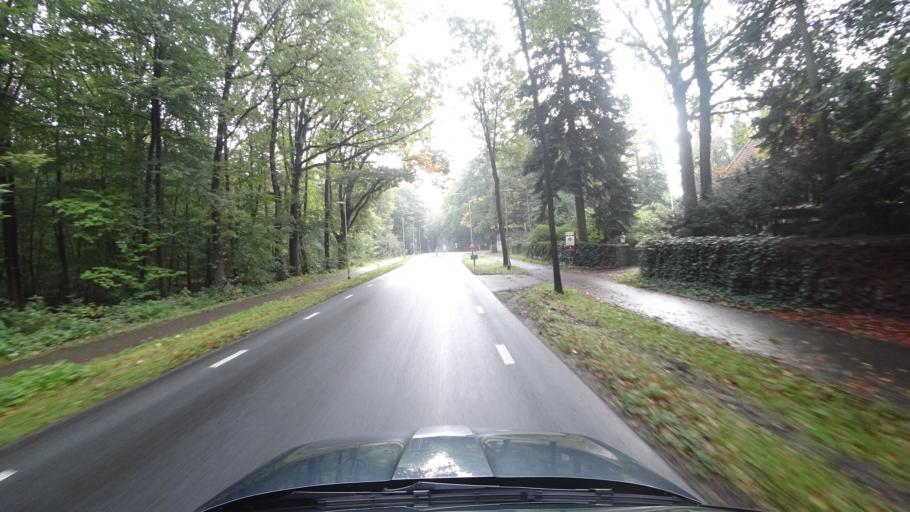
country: NL
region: Gelderland
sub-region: Gemeente Ede
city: Bennekom
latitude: 51.9938
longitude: 5.6941
